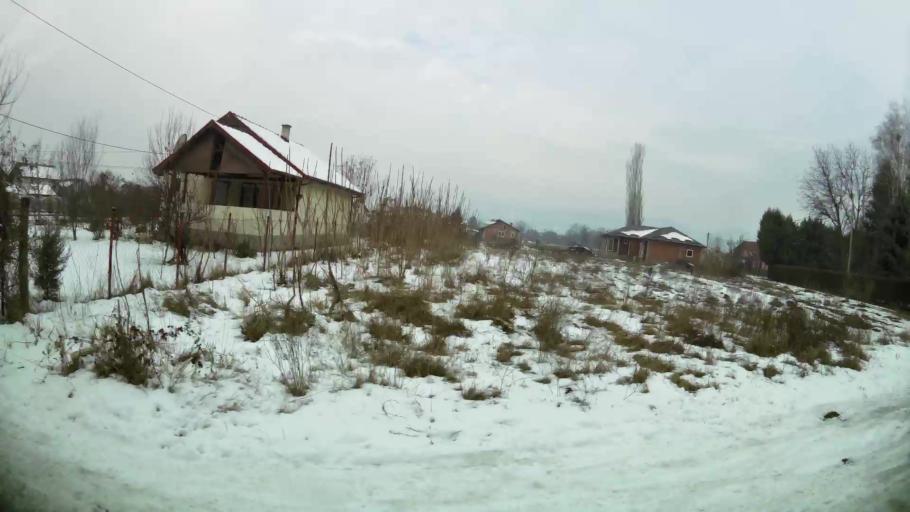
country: MK
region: Saraj
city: Saraj
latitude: 42.0489
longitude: 21.3593
